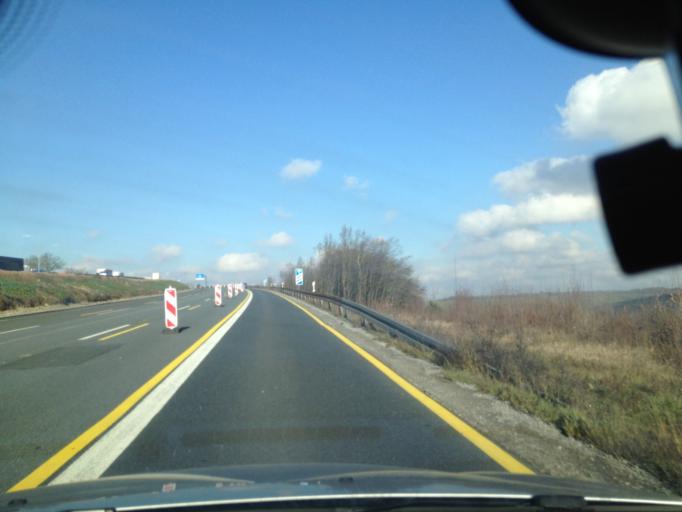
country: DE
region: Bavaria
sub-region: Regierungsbezirk Unterfranken
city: Randersacker
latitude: 49.7493
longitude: 9.9655
